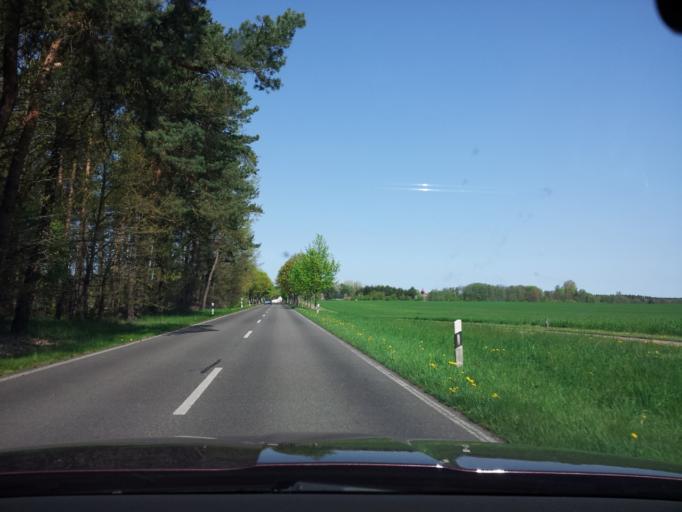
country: DE
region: Brandenburg
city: Juterbog
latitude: 52.0144
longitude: 13.0636
